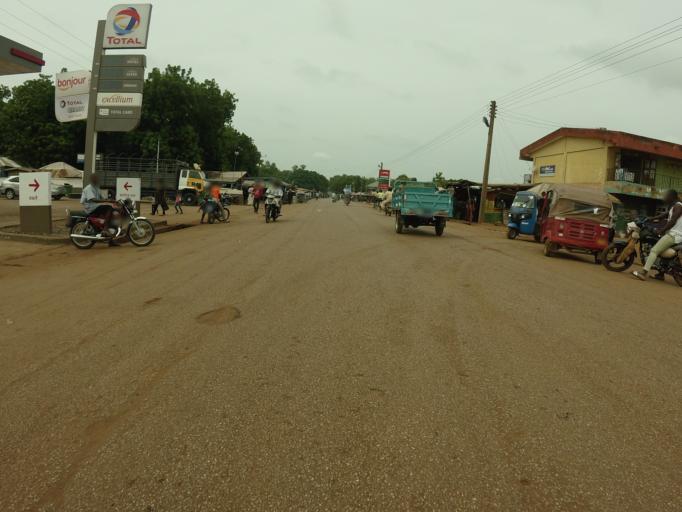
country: GH
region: Northern
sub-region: Yendi
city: Yendi
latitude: 9.4401
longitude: -0.0069
